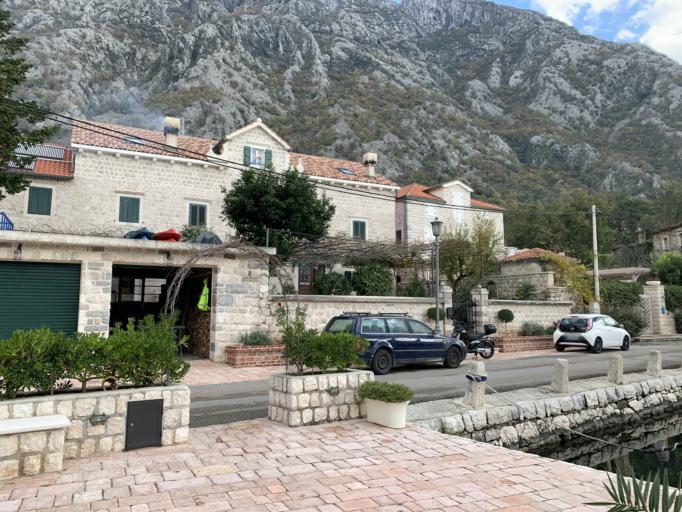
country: ME
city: Dobrota
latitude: 42.4808
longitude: 18.7637
